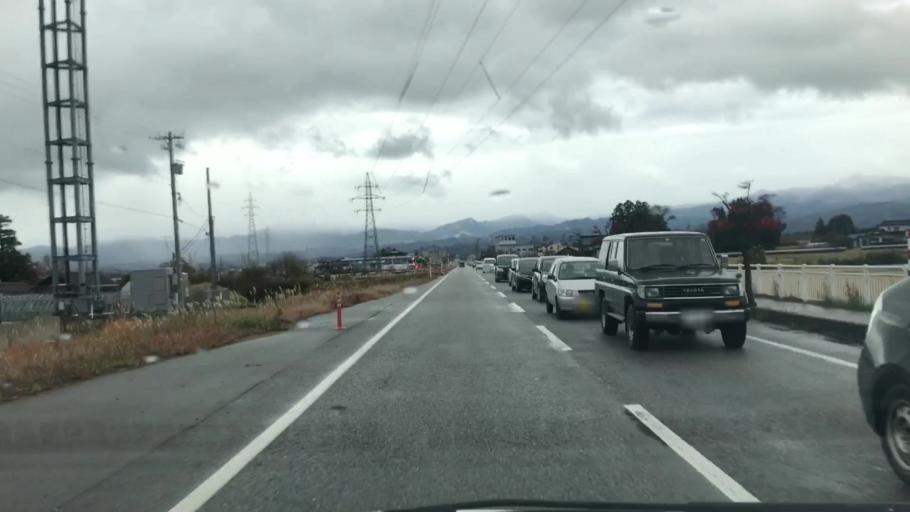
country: JP
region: Toyama
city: Kamiichi
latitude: 36.6867
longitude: 137.3049
